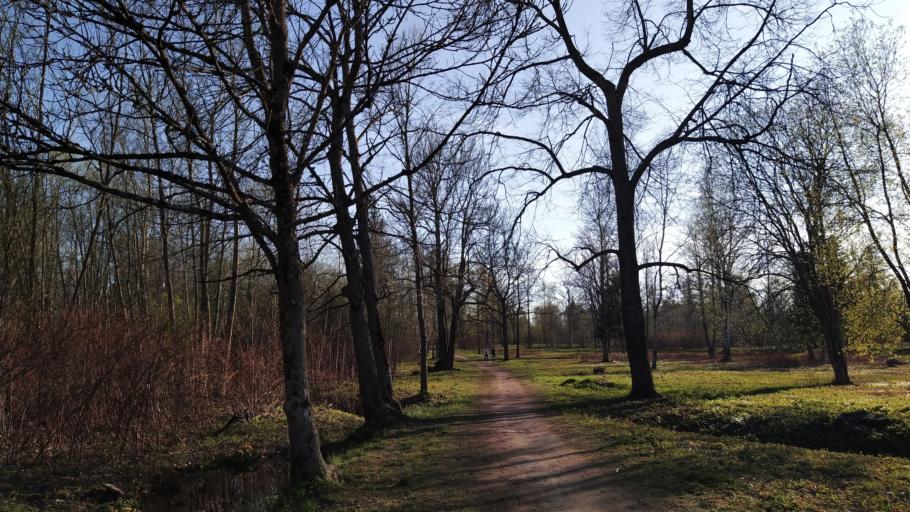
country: RU
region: St.-Petersburg
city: Aleksandrovskaya
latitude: 59.7075
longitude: 30.3506
